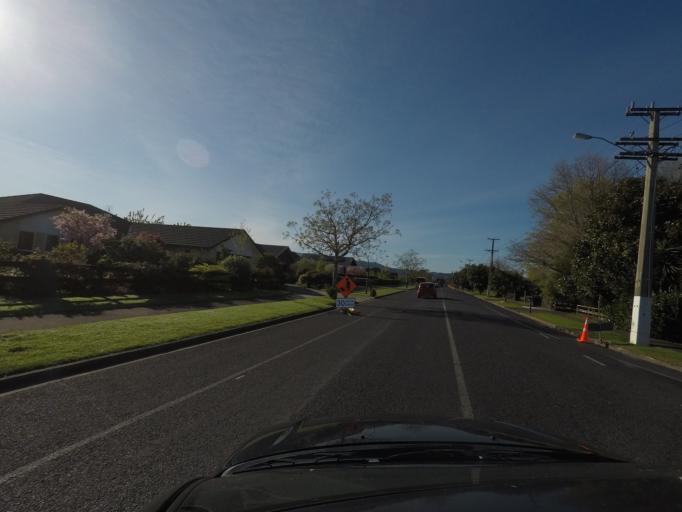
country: NZ
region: Auckland
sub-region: Auckland
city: Red Hill
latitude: -36.9970
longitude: 175.0376
